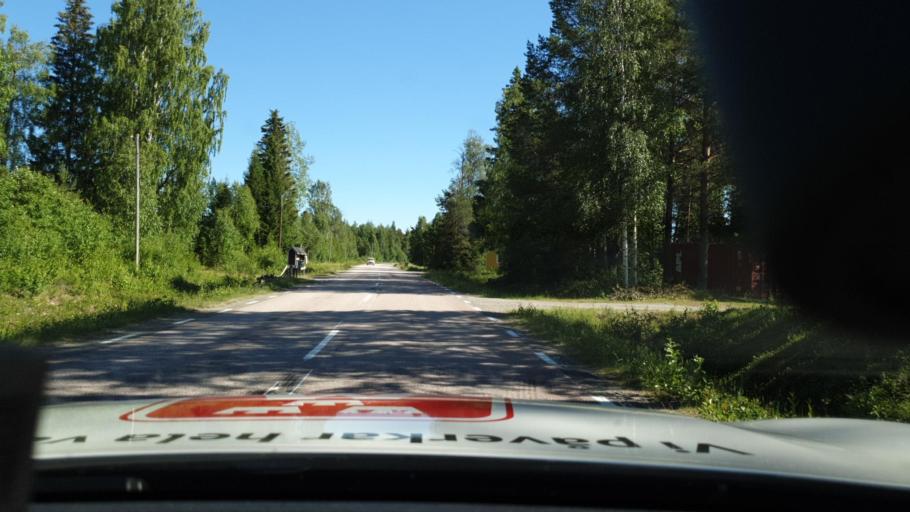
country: SE
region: Norrbotten
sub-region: Lulea Kommun
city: Ranea
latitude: 65.9198
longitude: 22.4432
